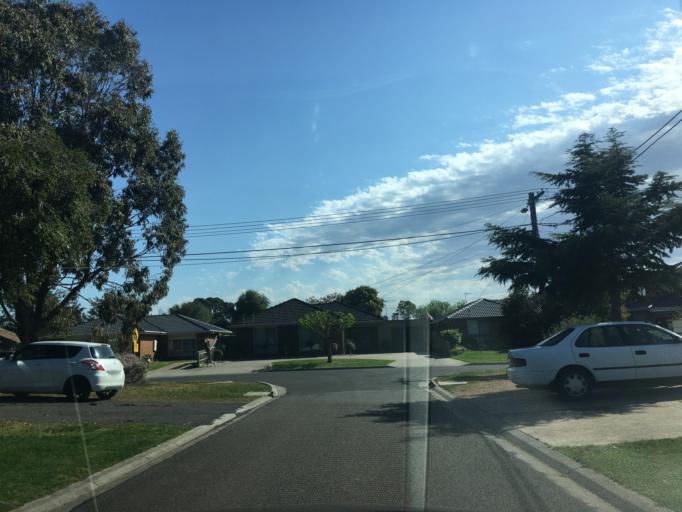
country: AU
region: Victoria
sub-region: Wyndham
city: Hoppers Crossing
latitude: -37.8730
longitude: 144.7044
